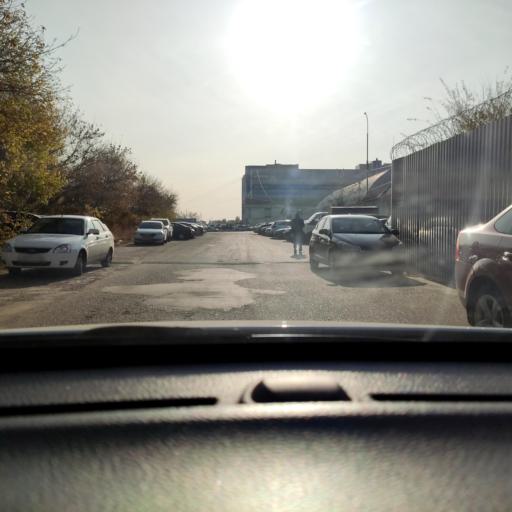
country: RU
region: Voronezj
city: Voronezh
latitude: 51.6624
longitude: 39.1273
